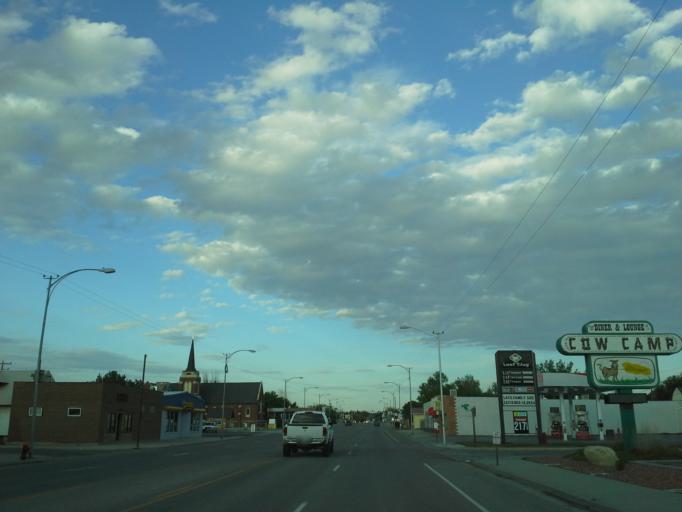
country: US
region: Wyoming
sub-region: Washakie County
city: Worland
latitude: 44.0168
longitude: -107.9537
